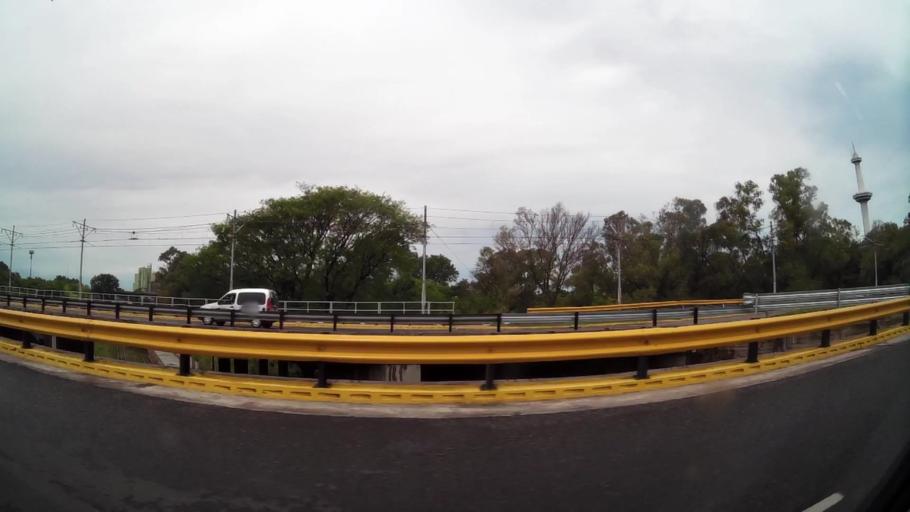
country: AR
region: Buenos Aires F.D.
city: Villa Lugano
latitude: -34.6672
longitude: -58.4522
